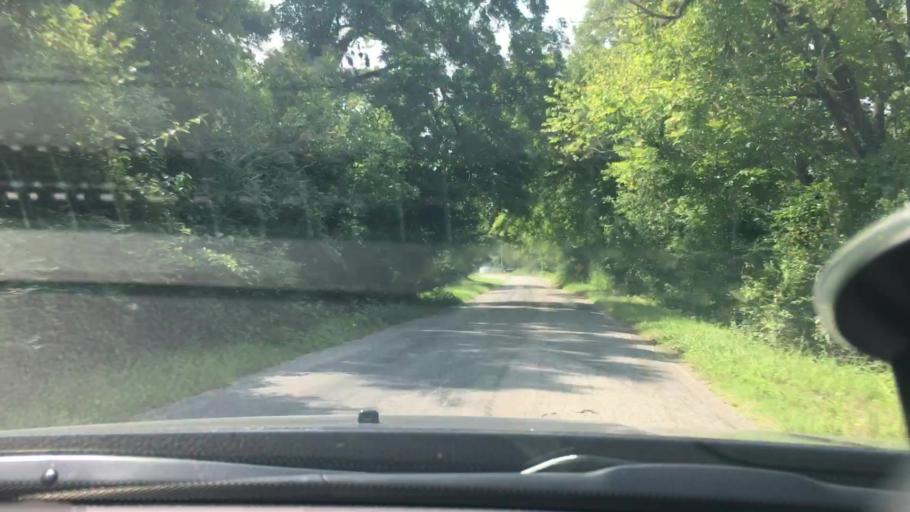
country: US
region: Oklahoma
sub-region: Pontotoc County
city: Ada
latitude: 34.6572
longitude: -96.5297
